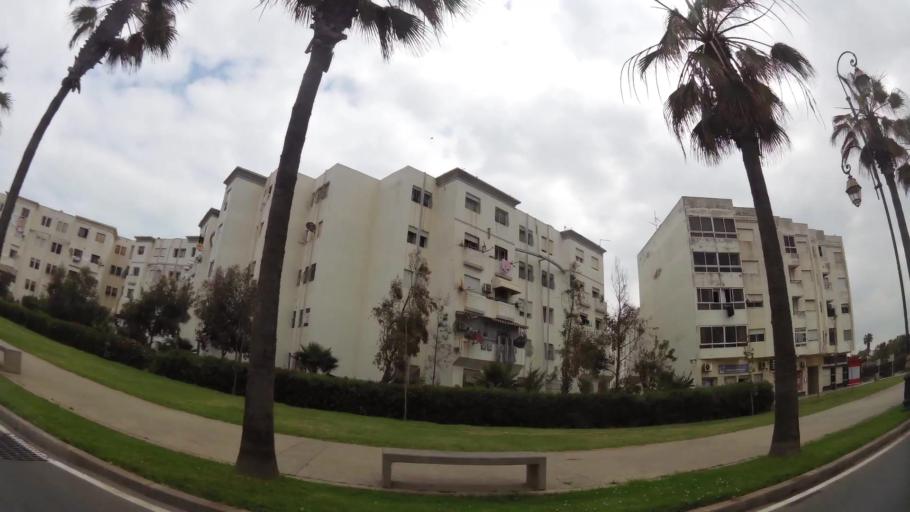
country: MA
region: Rabat-Sale-Zemmour-Zaer
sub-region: Rabat
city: Rabat
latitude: 33.9903
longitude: -6.8828
